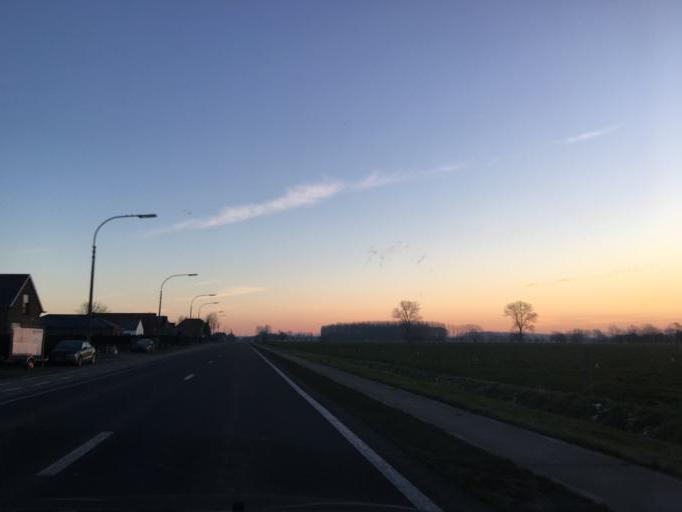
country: BE
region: Flanders
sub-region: Provincie Oost-Vlaanderen
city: Aalter
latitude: 51.1171
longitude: 3.4533
